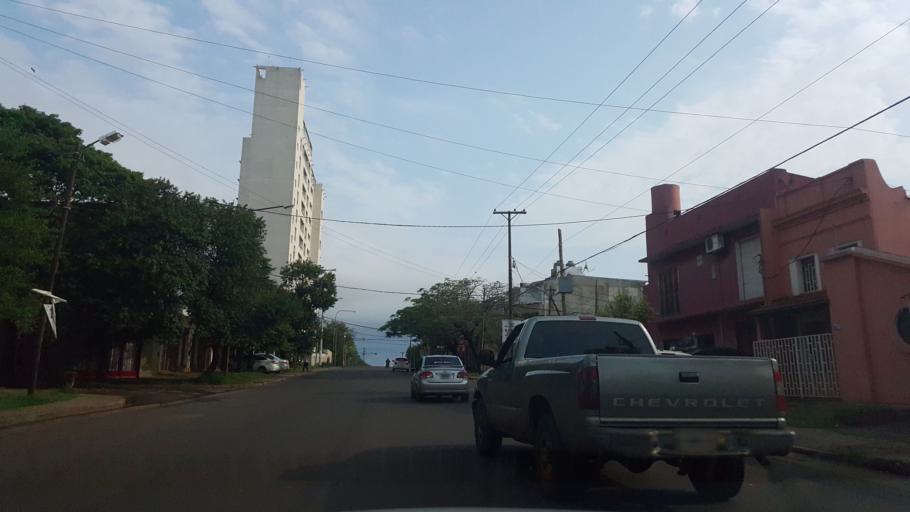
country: AR
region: Misiones
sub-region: Departamento de Capital
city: Posadas
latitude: -27.3809
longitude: -55.8881
